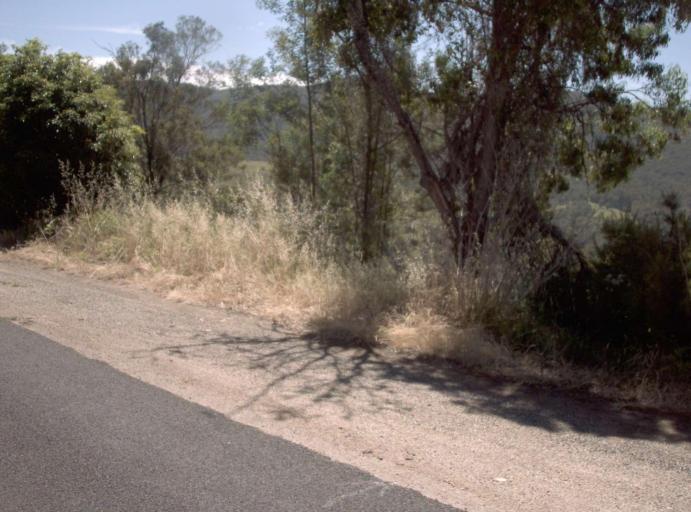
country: AU
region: Victoria
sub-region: East Gippsland
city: Lakes Entrance
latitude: -37.4256
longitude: 148.2015
